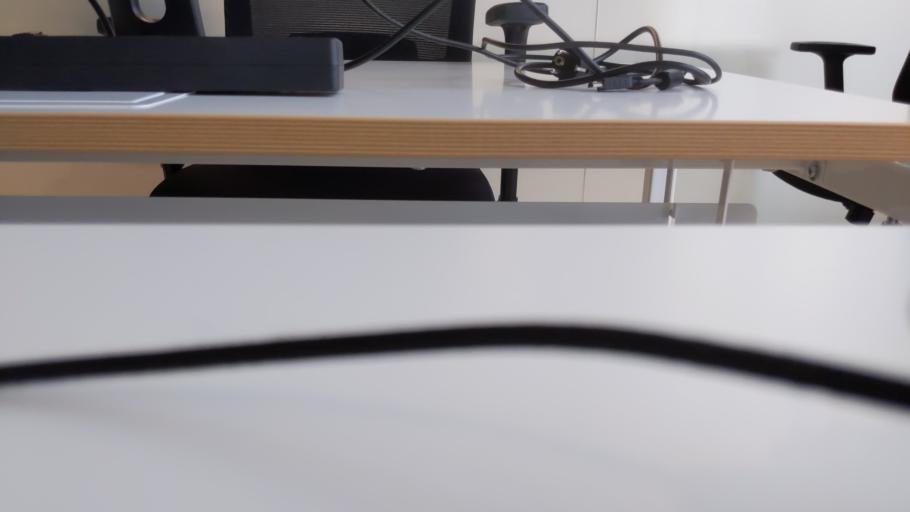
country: RU
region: Moskovskaya
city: Rogachevo
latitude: 56.4156
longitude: 37.0326
